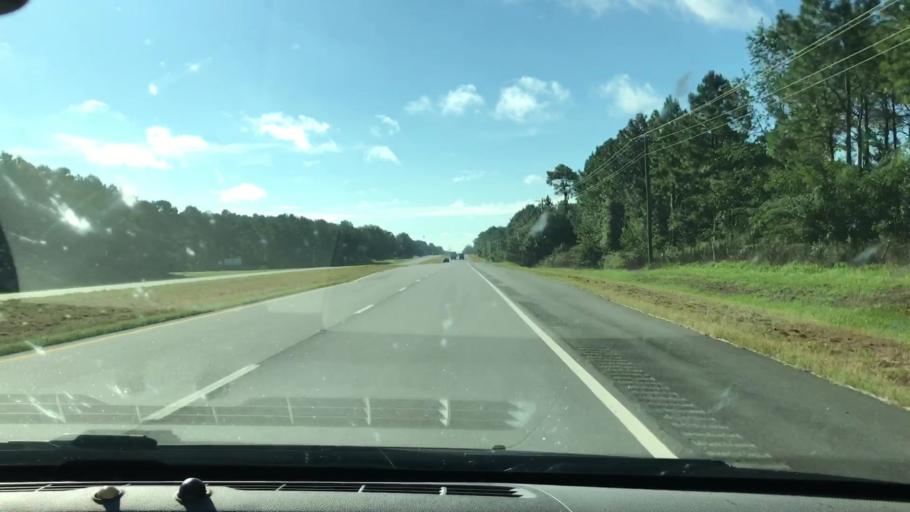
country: US
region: Georgia
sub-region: Lee County
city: Leesburg
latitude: 31.6744
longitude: -84.2929
